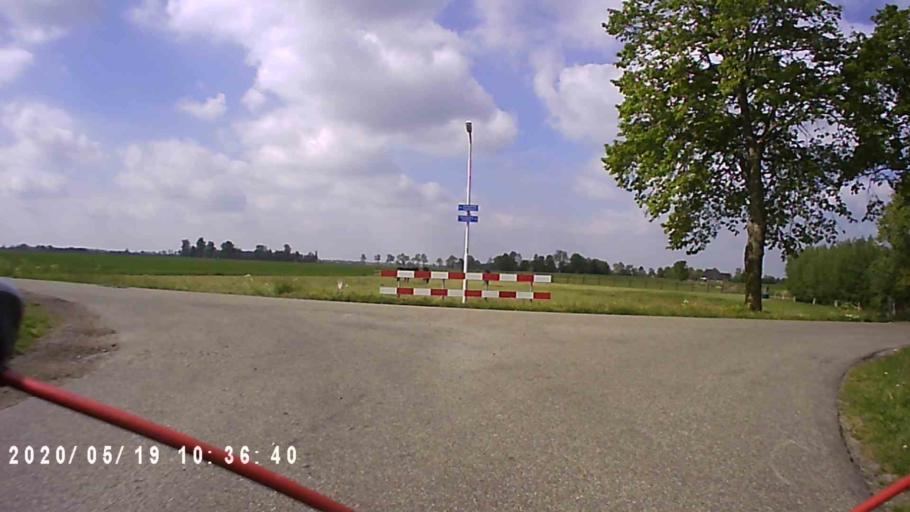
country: NL
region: Friesland
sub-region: Gemeente Kollumerland en Nieuwkruisland
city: Kollum
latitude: 53.2771
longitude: 6.1812
